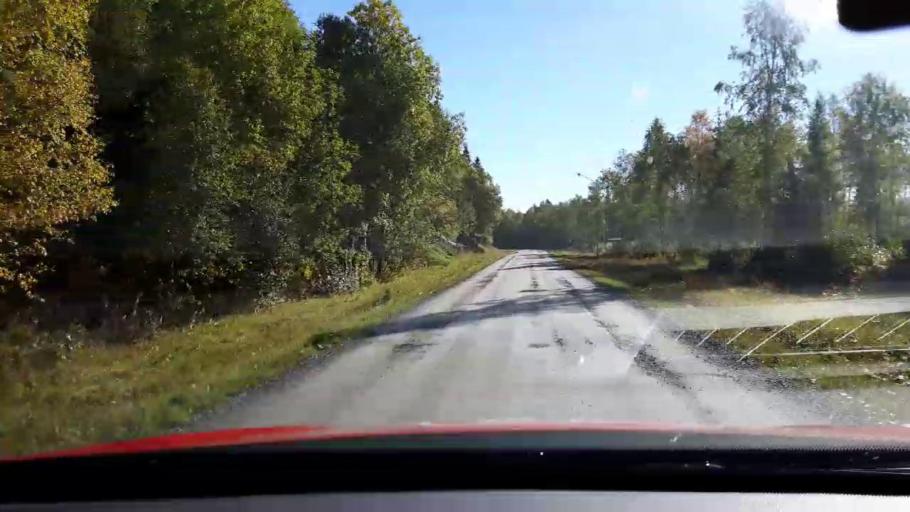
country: NO
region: Nord-Trondelag
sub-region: Lierne
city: Sandvika
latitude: 64.6478
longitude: 13.7578
